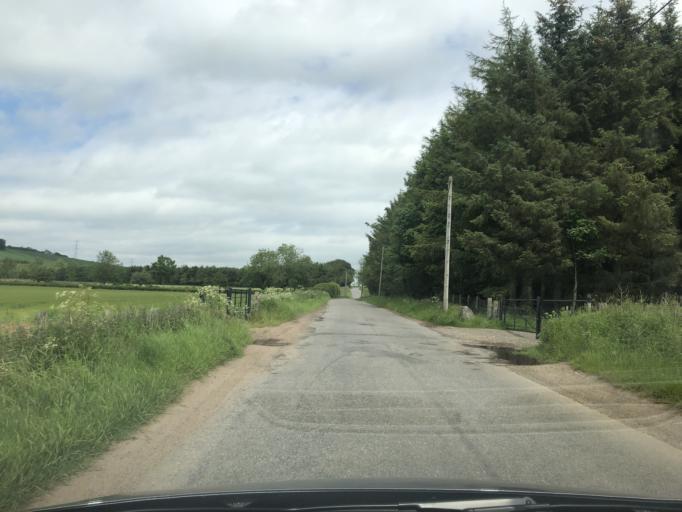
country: GB
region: Scotland
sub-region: Angus
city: Kirriemuir
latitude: 56.7200
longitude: -2.9330
